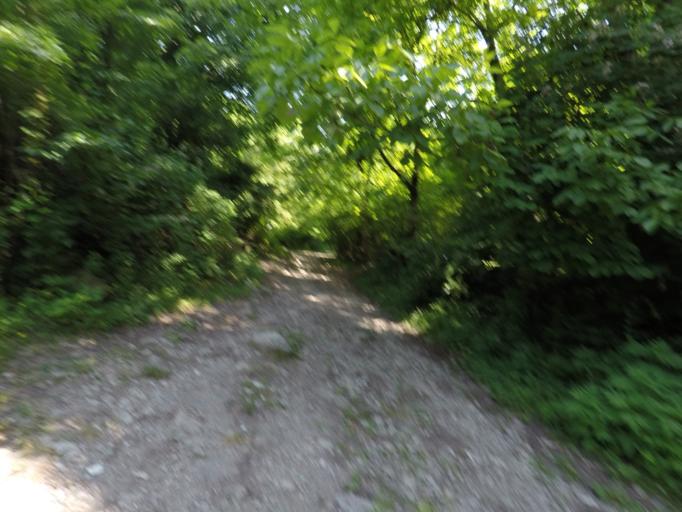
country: AZ
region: Qakh Rayon
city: Cinarli
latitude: 41.4904
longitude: 46.8580
